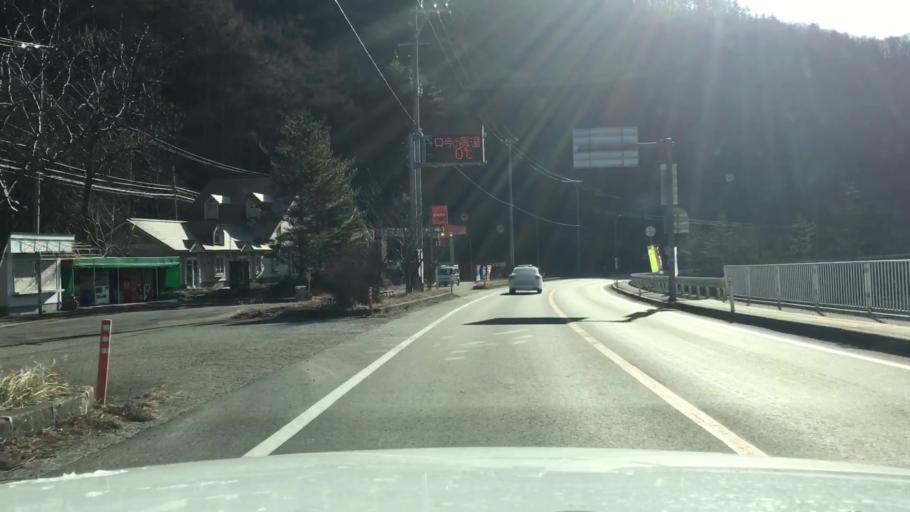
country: JP
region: Iwate
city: Tono
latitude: 39.6414
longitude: 141.5990
